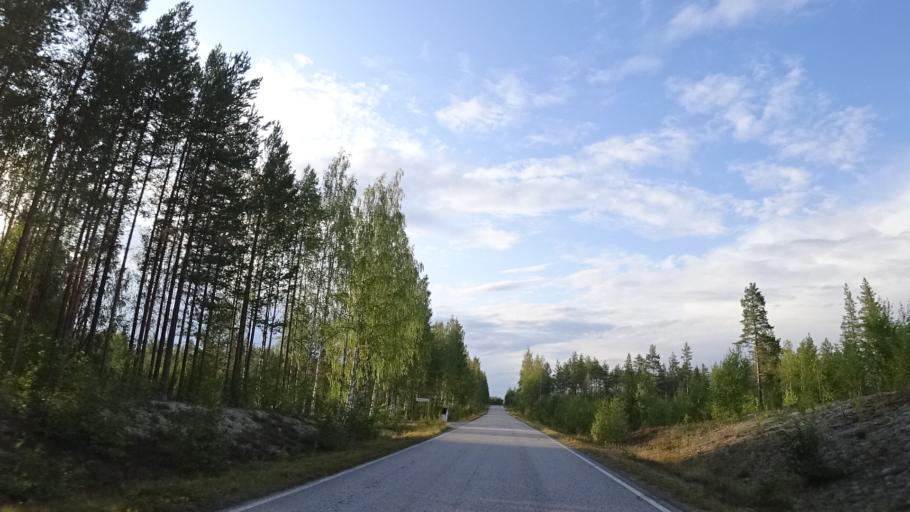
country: FI
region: North Karelia
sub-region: Pielisen Karjala
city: Lieksa
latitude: 63.3515
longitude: 30.2653
